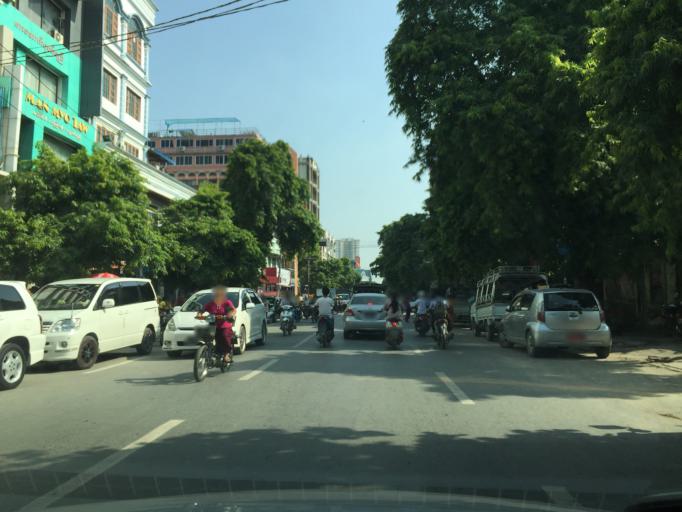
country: MM
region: Mandalay
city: Mandalay
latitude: 21.9739
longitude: 96.0773
